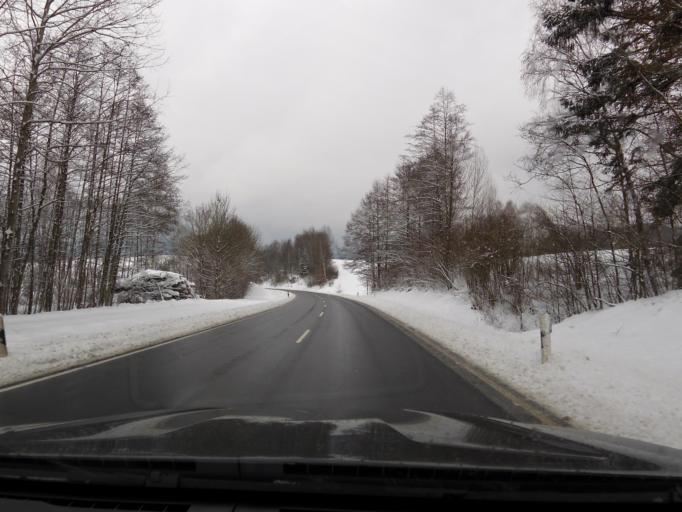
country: DE
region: Bavaria
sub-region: Lower Bavaria
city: Lalling
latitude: 48.8270
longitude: 13.1458
